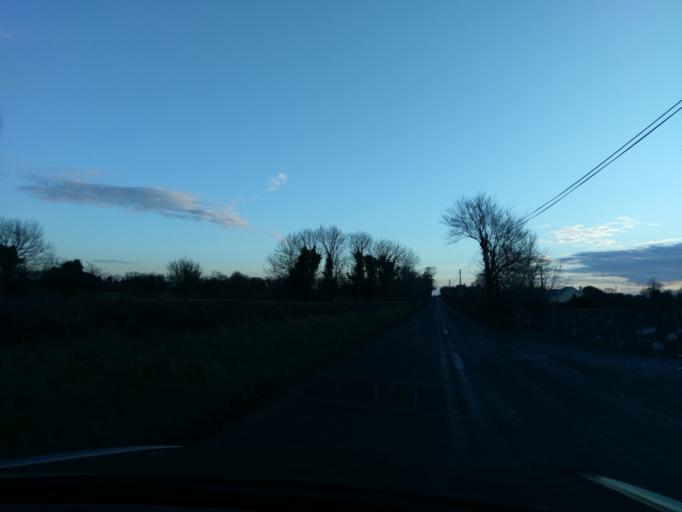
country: IE
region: Connaught
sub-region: County Galway
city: Athenry
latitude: 53.2988
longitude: -8.6276
